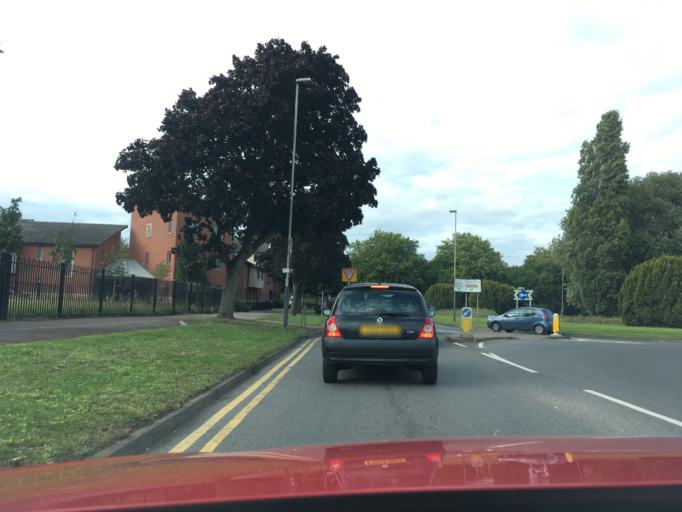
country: GB
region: England
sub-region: Gloucestershire
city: Uckington
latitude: 51.9026
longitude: -2.1162
